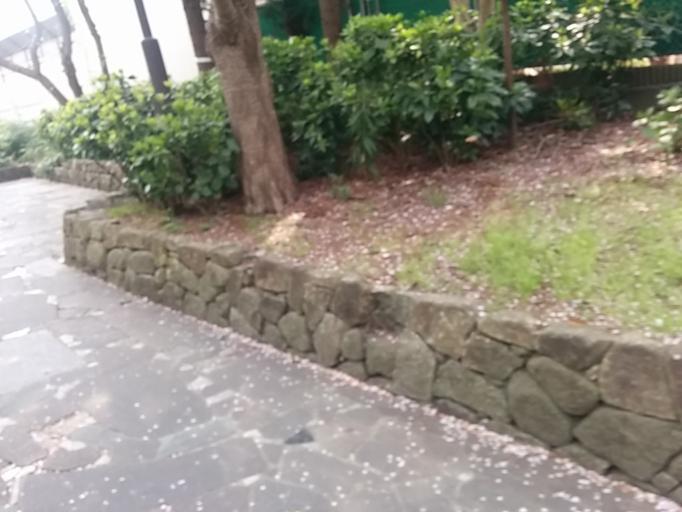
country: JP
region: Tokyo
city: Urayasu
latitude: 35.6549
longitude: 139.8581
